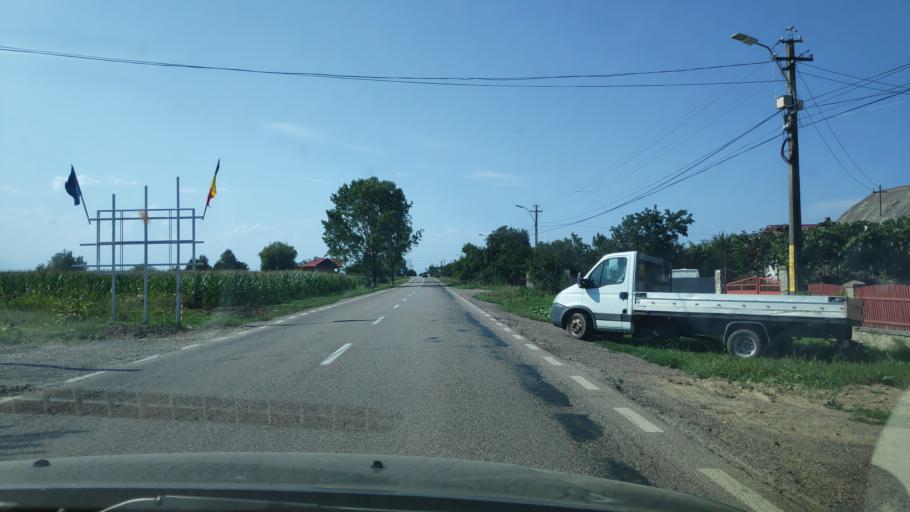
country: RO
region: Suceava
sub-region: Comuna Boroaia
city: Boroaia
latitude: 47.3771
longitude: 26.3216
